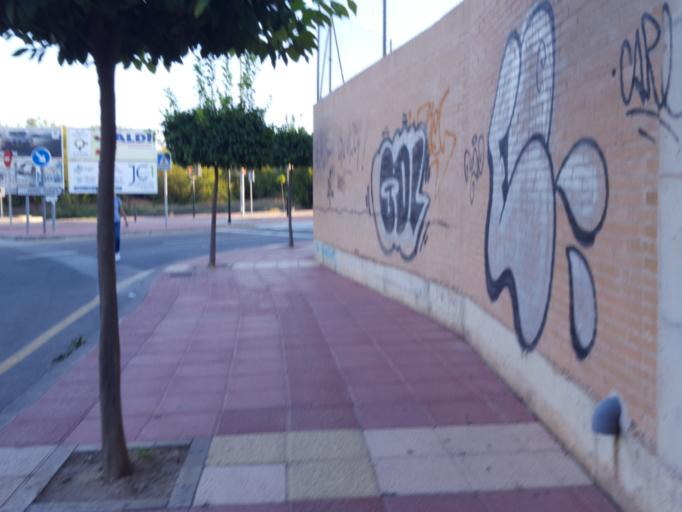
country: ES
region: Murcia
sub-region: Murcia
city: Murcia
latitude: 38.0073
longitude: -1.1508
